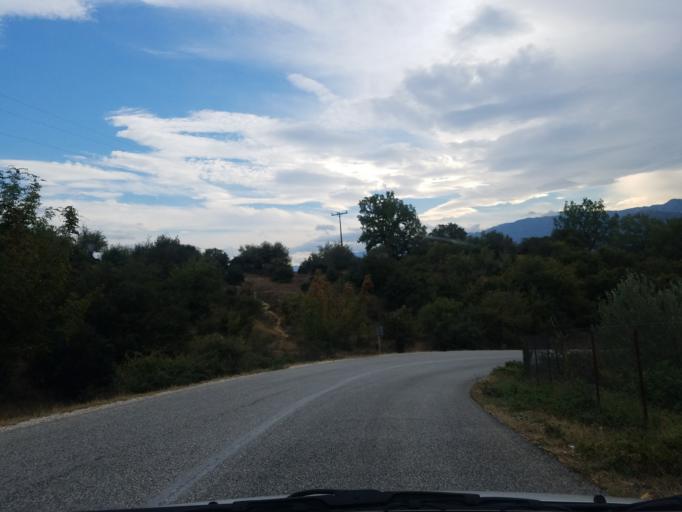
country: GR
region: Thessaly
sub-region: Trikala
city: Kalampaka
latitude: 39.7040
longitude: 21.6512
